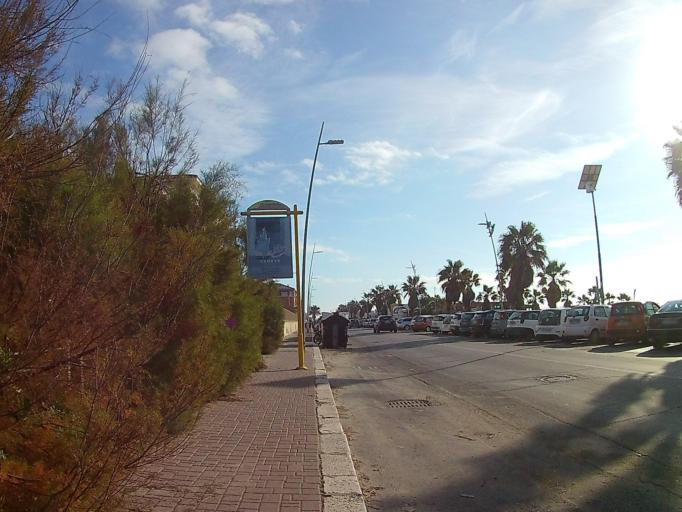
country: IT
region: Latium
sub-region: Citta metropolitana di Roma Capitale
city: Lido di Ostia
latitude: 41.7333
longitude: 12.2656
